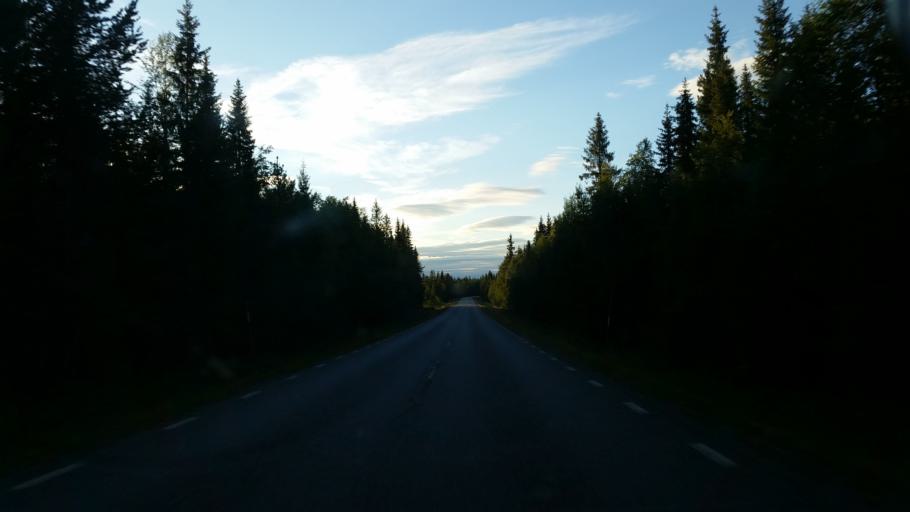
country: SE
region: Vaesterbotten
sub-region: Storumans Kommun
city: Storuman
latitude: 64.8799
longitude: 16.9873
